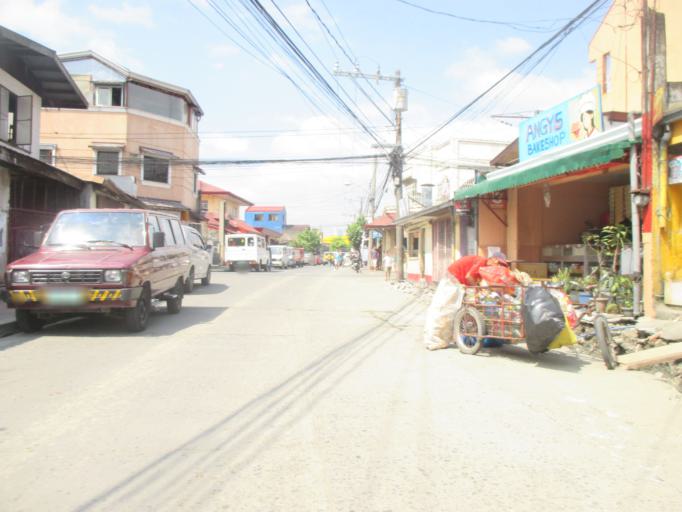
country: PH
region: Metro Manila
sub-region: Marikina
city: Calumpang
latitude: 14.6237
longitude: 121.0990
